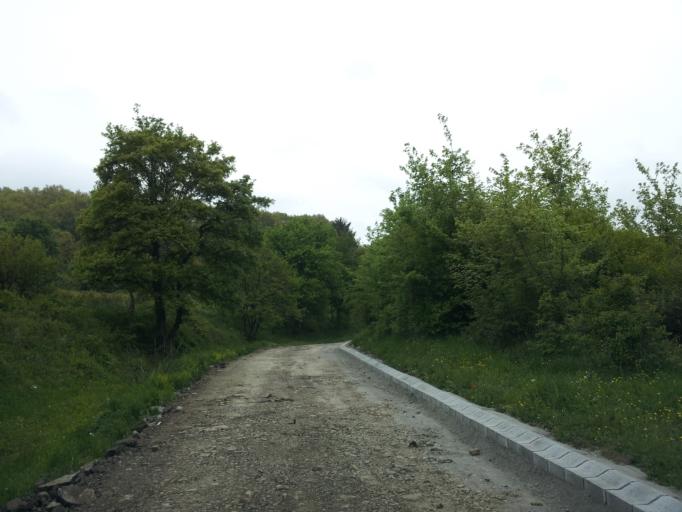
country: HU
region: Baranya
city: Hosszuheteny
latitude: 46.1864
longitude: 18.3570
